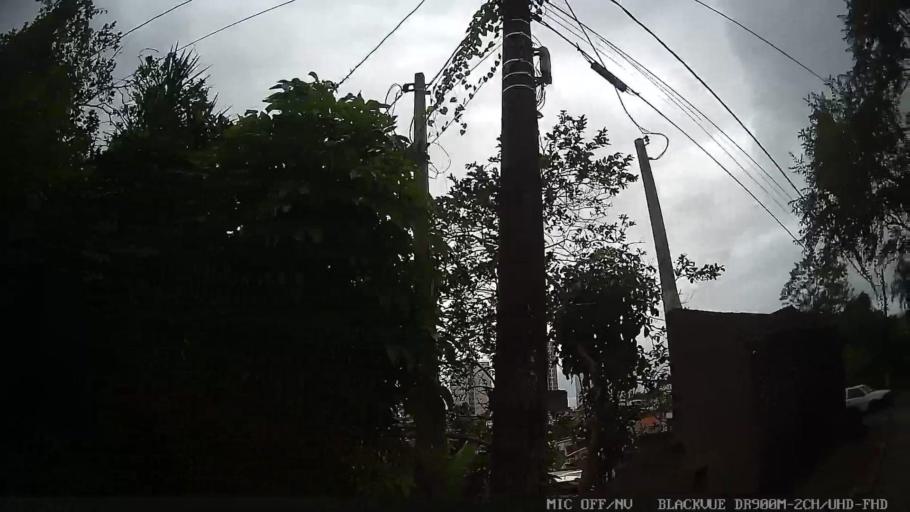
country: BR
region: Sao Paulo
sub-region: Itanhaem
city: Itanhaem
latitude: -24.1916
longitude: -46.8030
